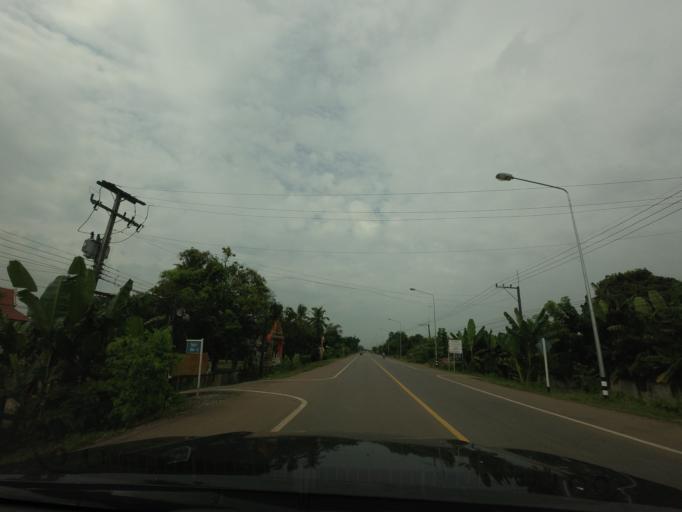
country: TH
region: Nong Khai
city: Nong Khai
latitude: 17.8109
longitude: 102.6976
